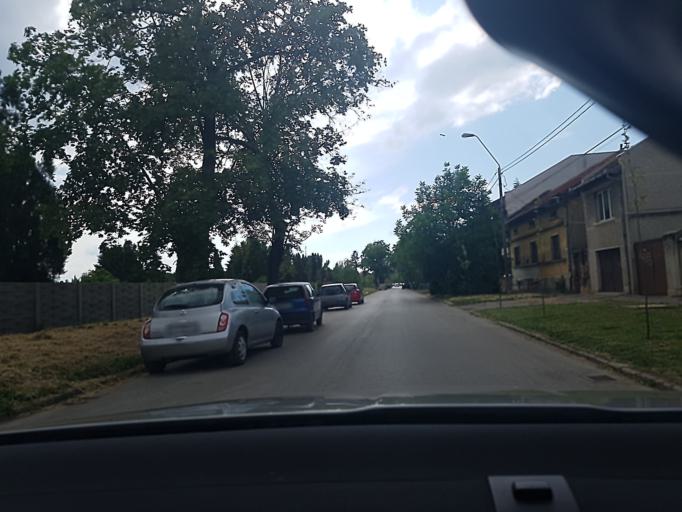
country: RO
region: Timis
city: Timisoara
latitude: 45.7379
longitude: 21.2218
